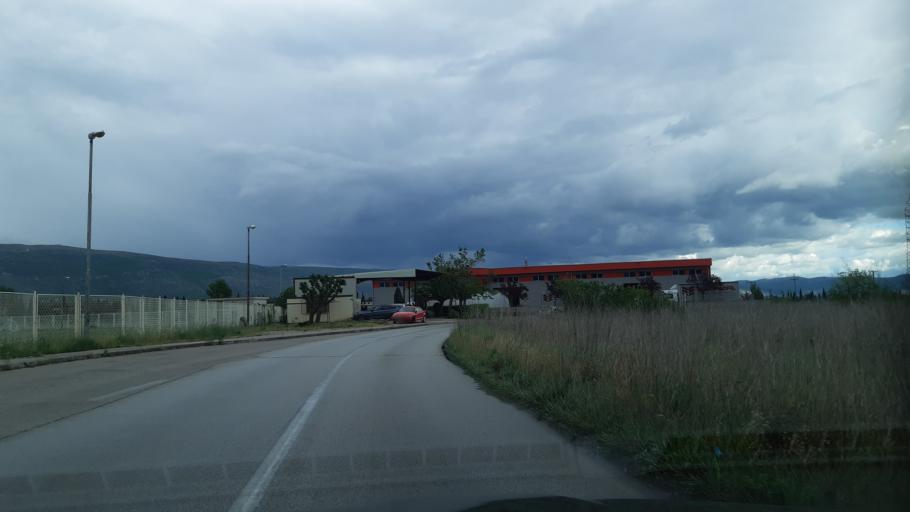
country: BA
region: Federation of Bosnia and Herzegovina
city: Rodoc
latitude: 43.3054
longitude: 17.8011
